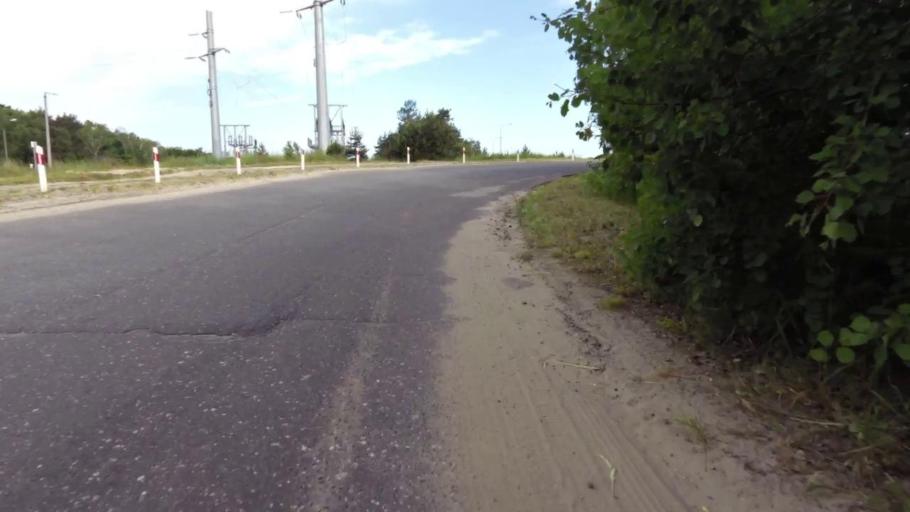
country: PL
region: West Pomeranian Voivodeship
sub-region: Swinoujscie
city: Swinoujscie
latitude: 53.9034
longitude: 14.2961
